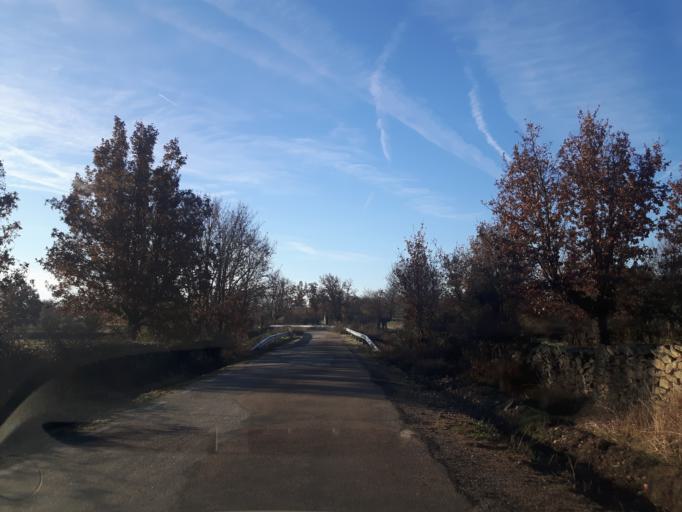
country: ES
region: Castille and Leon
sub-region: Provincia de Salamanca
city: Cerralbo
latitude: 40.9396
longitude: -6.6196
